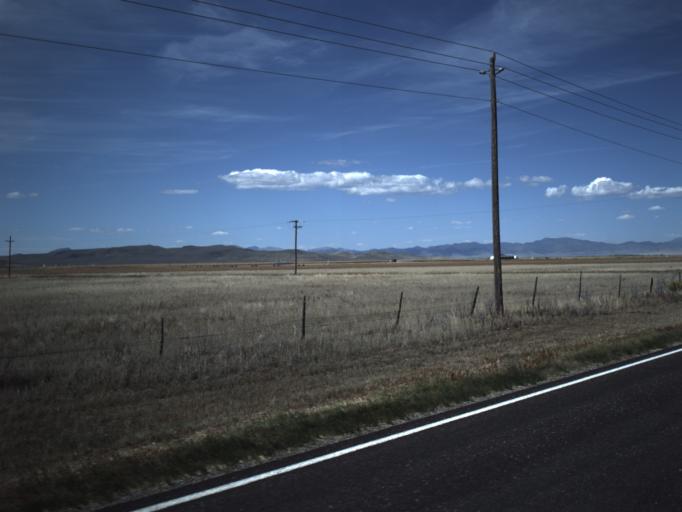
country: US
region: Utah
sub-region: Washington County
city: Enterprise
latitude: 37.6473
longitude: -113.6612
